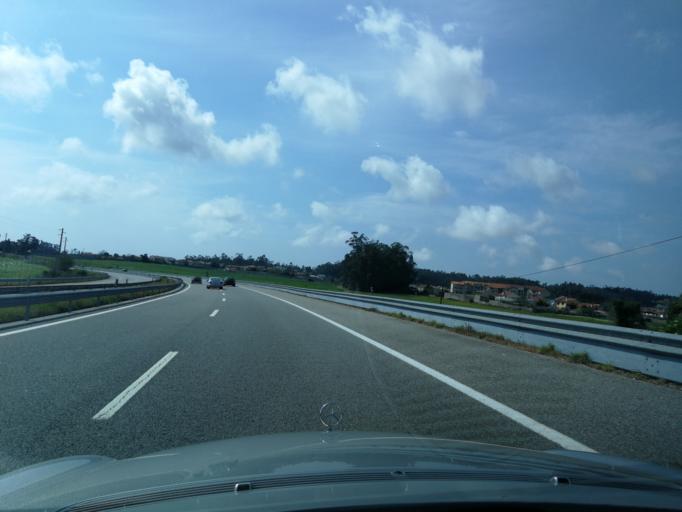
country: PT
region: Porto
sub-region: Vila do Conde
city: Arvore
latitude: 41.3937
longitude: -8.6834
